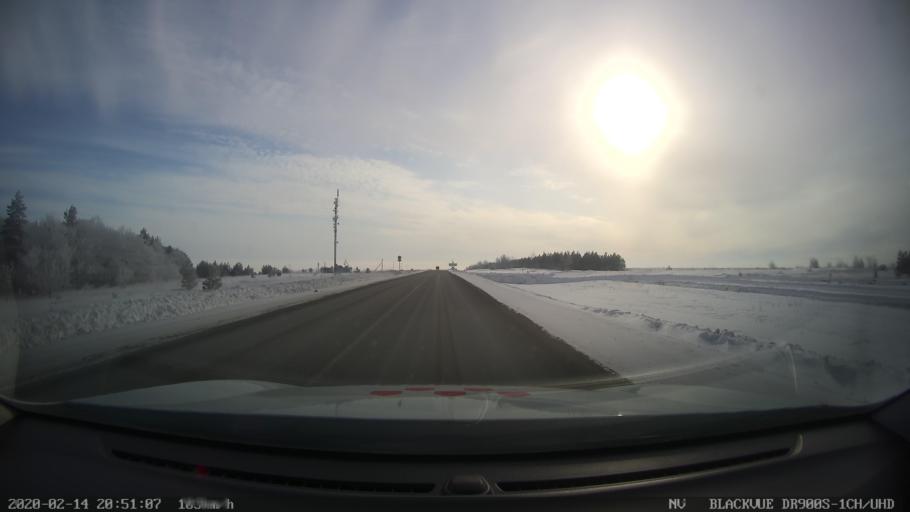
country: RU
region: Tatarstan
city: Kuybyshevskiy Zaton
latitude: 55.2167
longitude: 49.2339
